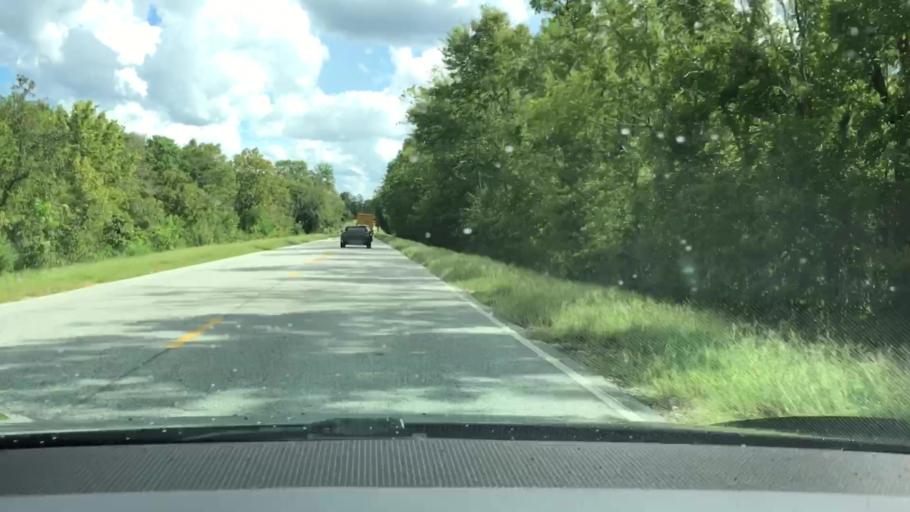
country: US
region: Alabama
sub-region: Montgomery County
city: Pike Road
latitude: 32.2214
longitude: -86.0908
